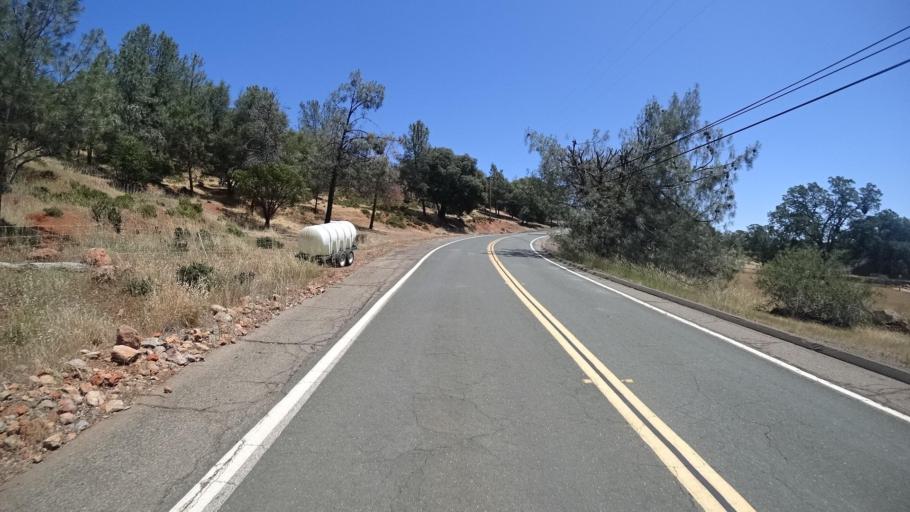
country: US
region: California
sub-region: Lake County
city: Hidden Valley Lake
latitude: 38.8193
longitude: -122.5660
